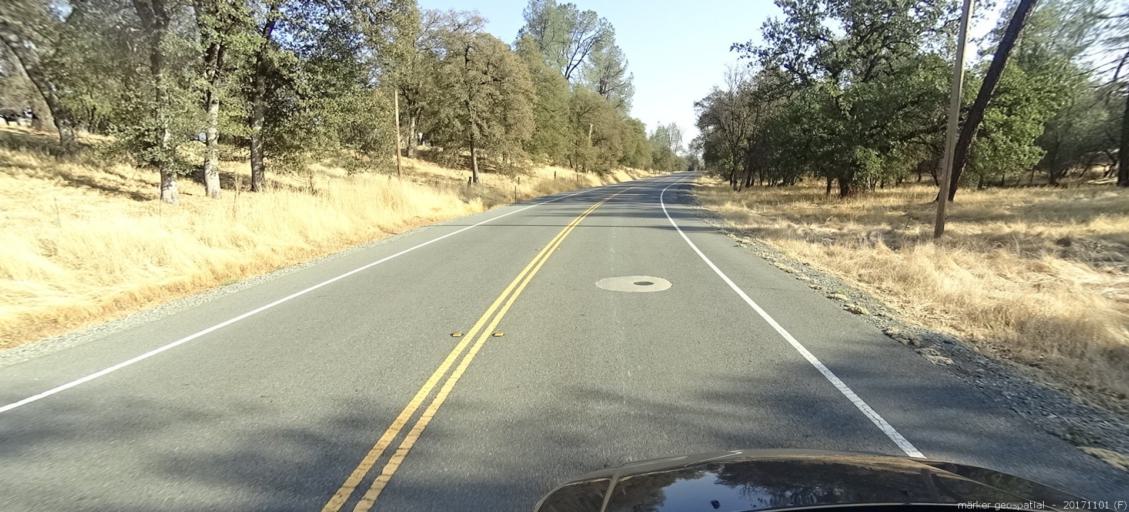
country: US
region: California
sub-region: Shasta County
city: Shasta Lake
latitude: 40.6507
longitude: -122.3328
